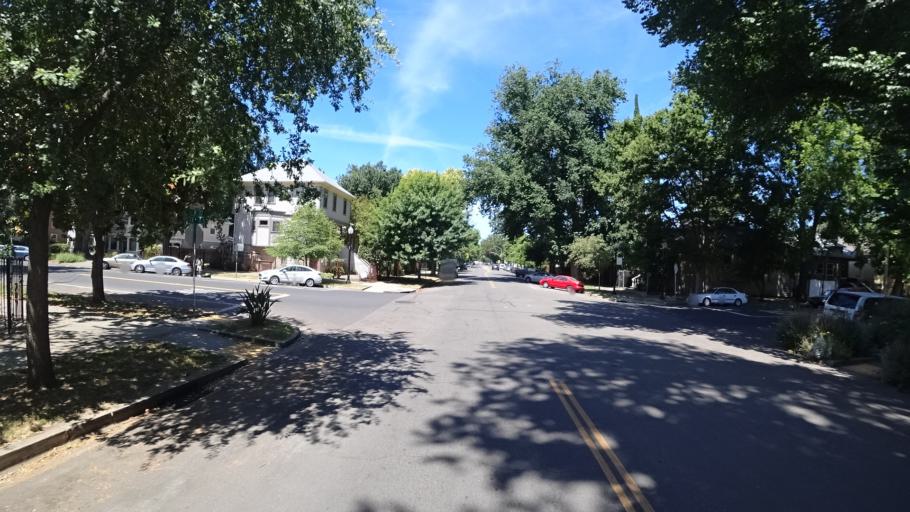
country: US
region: California
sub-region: Sacramento County
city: Sacramento
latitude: 38.5857
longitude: -121.4862
